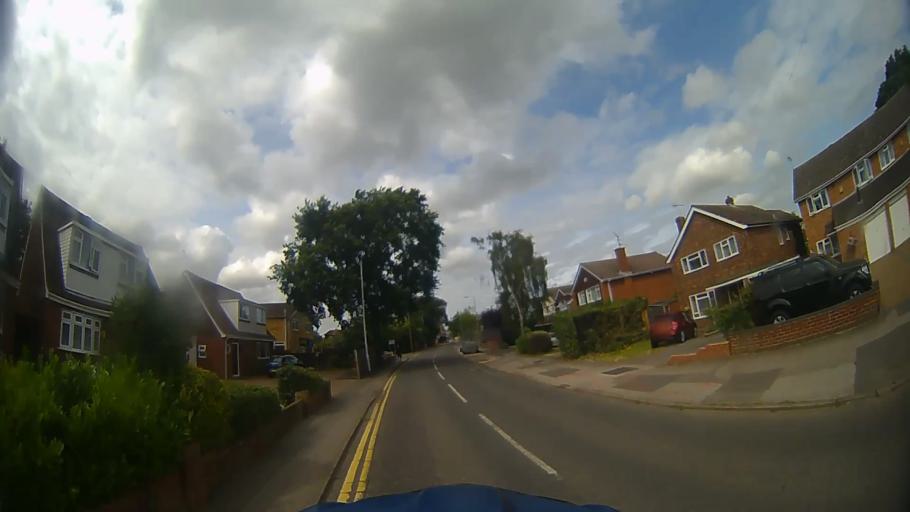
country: GB
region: England
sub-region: Wokingham
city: Earley
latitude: 51.4502
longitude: -0.9065
